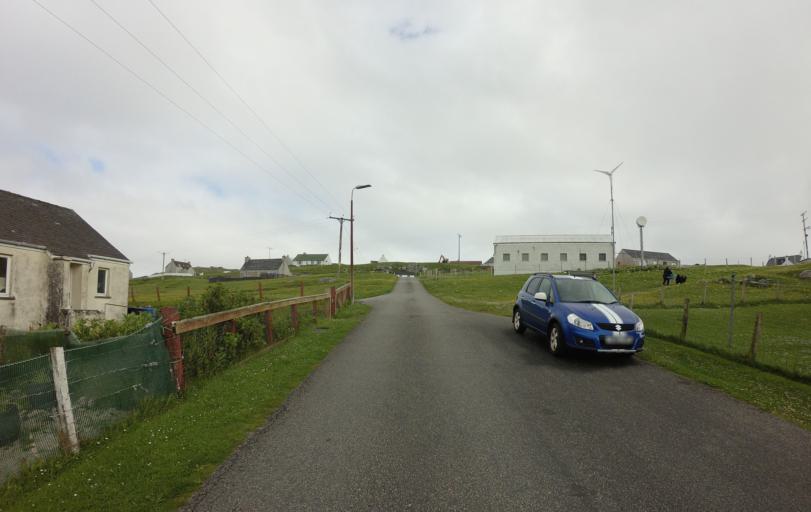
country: GB
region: Scotland
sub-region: Eilean Siar
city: Isle of South Uist
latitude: 57.0848
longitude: -7.3086
